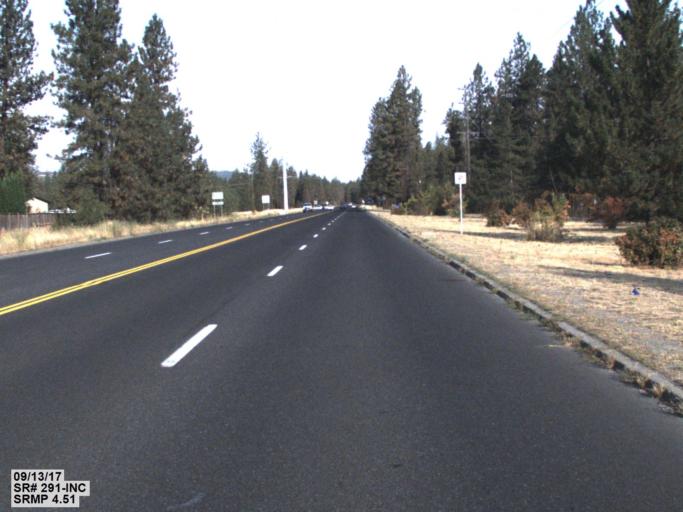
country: US
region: Washington
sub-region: Spokane County
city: Town and Country
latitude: 47.7289
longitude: -117.4995
